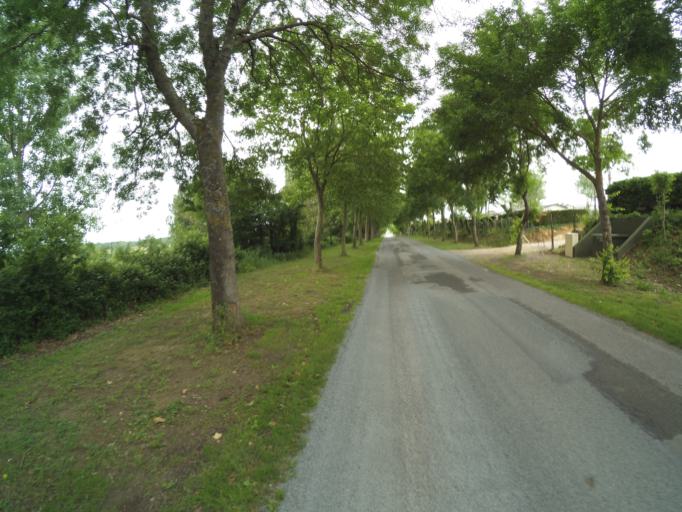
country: FR
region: Poitou-Charentes
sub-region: Departement de la Charente-Maritime
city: Saint-Laurent-de-la-Pree
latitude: 45.9891
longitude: -1.0171
